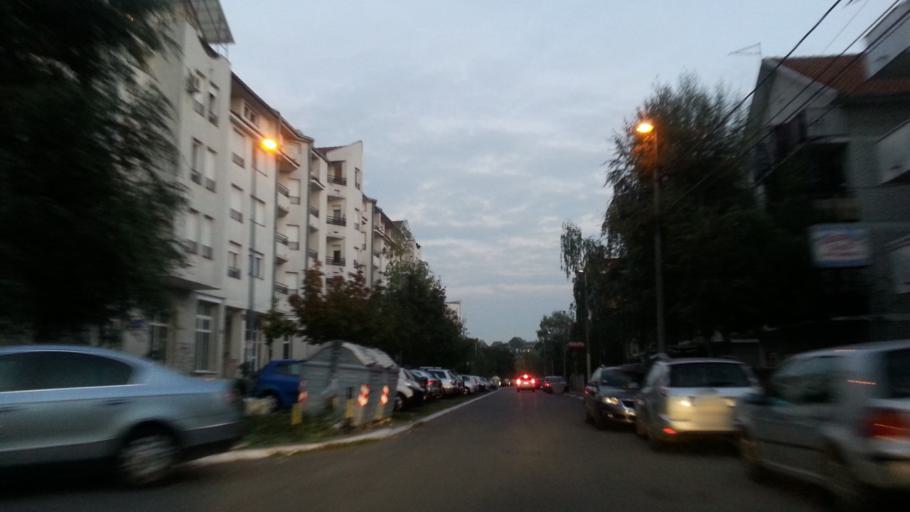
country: RS
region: Central Serbia
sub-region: Belgrade
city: Rakovica
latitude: 44.7576
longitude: 20.4254
